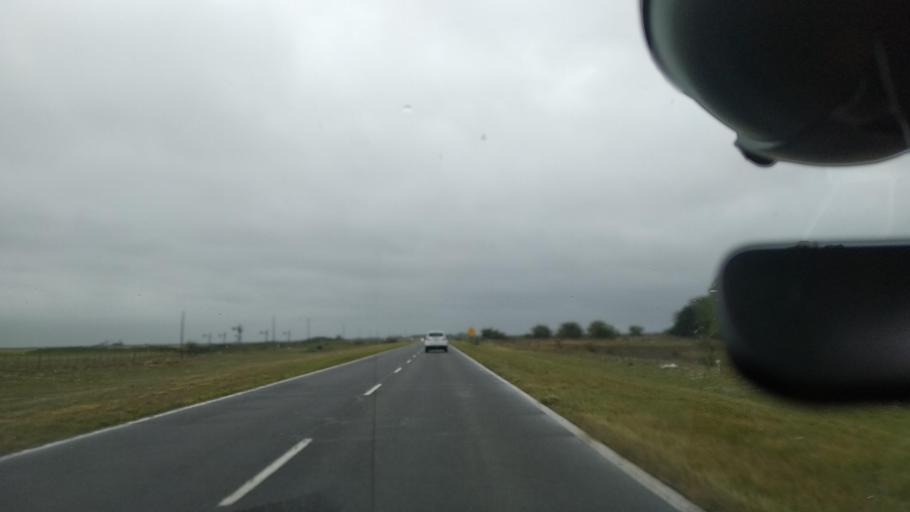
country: AR
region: Buenos Aires
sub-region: Partido de Dolores
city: Dolores
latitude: -36.0983
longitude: -57.4340
